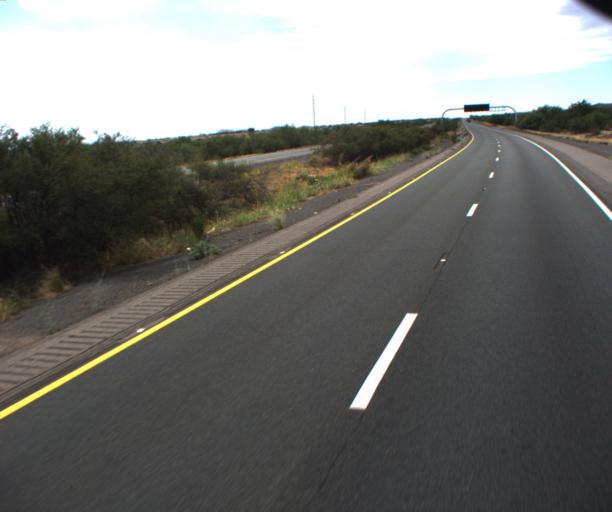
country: US
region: Arizona
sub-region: Yavapai County
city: Spring Valley
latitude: 34.3607
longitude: -112.1172
